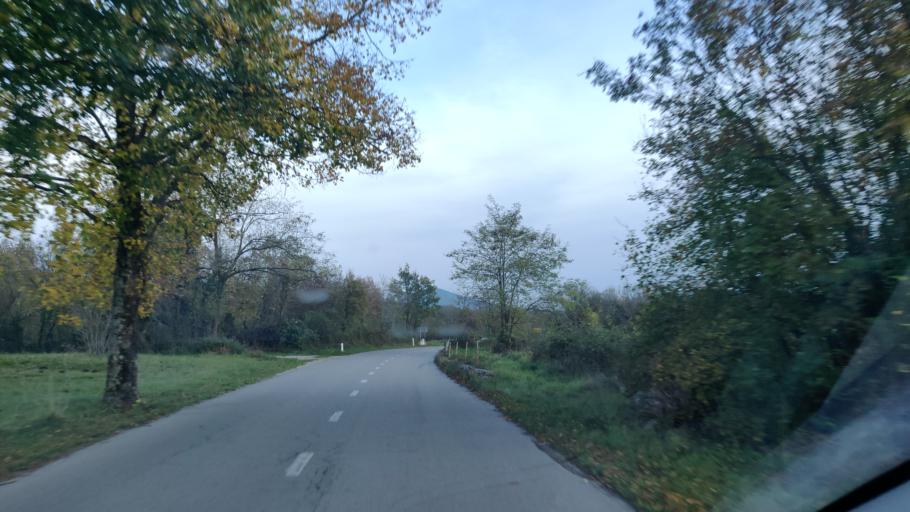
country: SI
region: Sezana
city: Sezana
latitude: 45.7595
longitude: 13.9136
